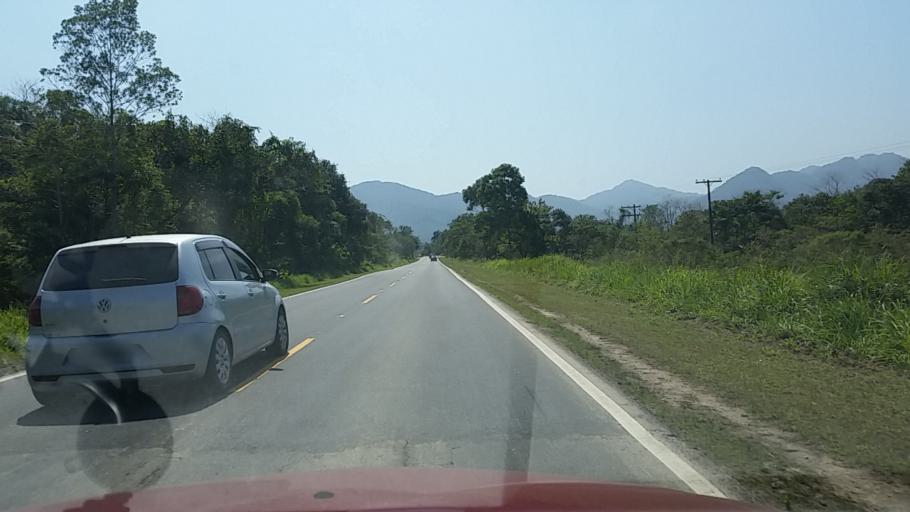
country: BR
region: Sao Paulo
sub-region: Juquia
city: Juquia
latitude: -24.4037
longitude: -47.5301
